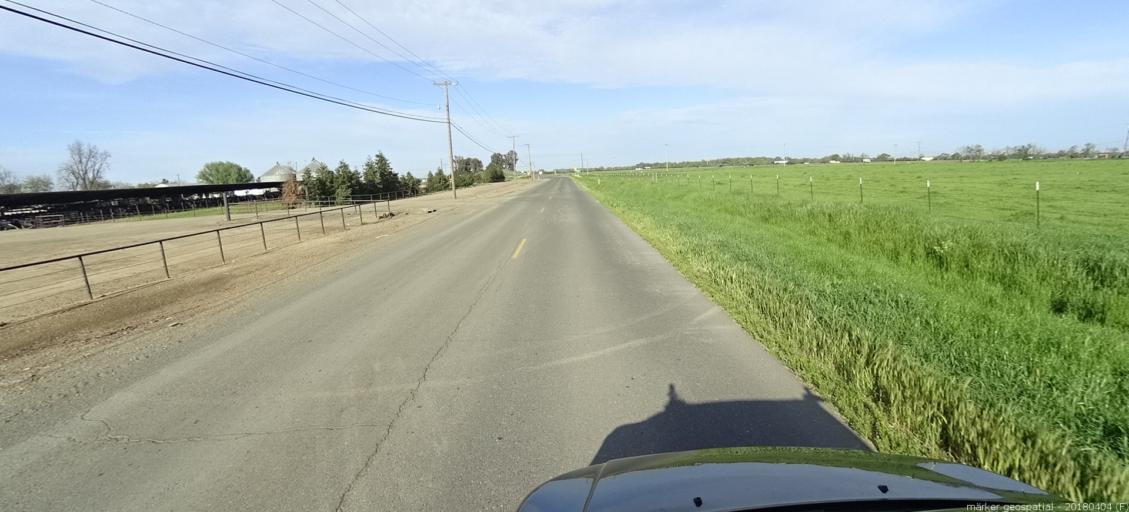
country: US
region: California
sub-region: Sacramento County
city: Galt
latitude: 38.3257
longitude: -121.3224
